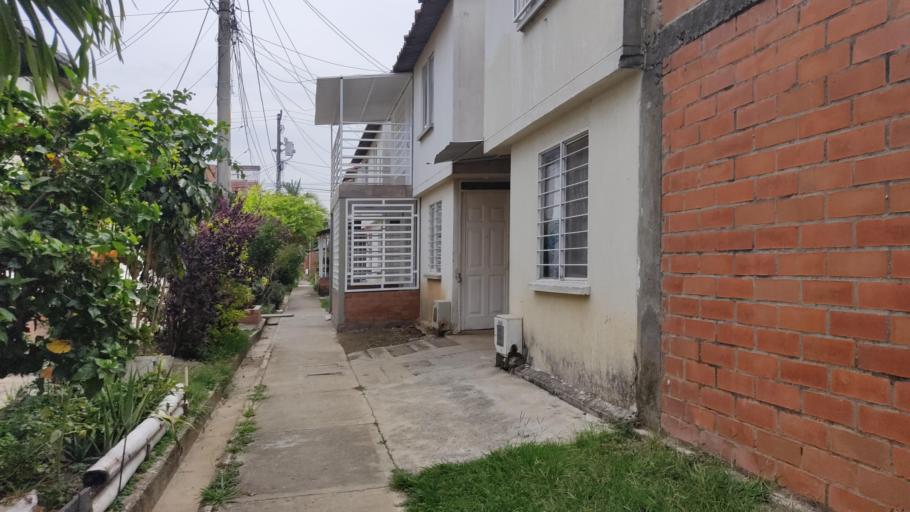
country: CO
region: Valle del Cauca
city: Jamundi
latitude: 3.2381
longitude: -76.5102
